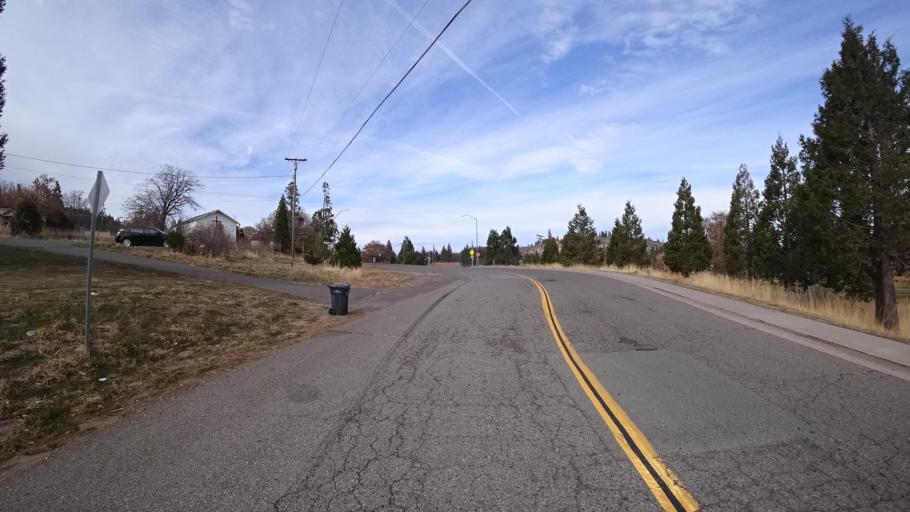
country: US
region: California
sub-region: Siskiyou County
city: Weed
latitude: 41.4361
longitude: -122.3864
